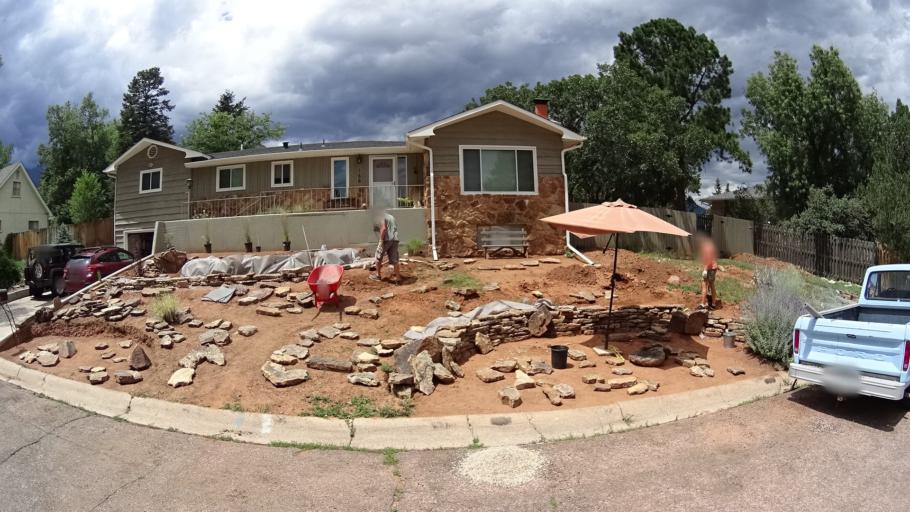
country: US
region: Colorado
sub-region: El Paso County
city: Manitou Springs
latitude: 38.8510
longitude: -104.8925
